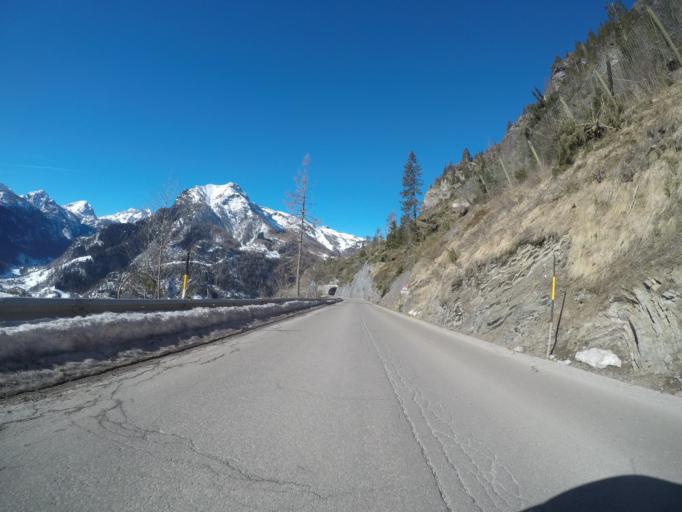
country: IT
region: Veneto
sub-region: Provincia di Belluno
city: Colle Santa Lucia
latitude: 46.4475
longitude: 11.9993
